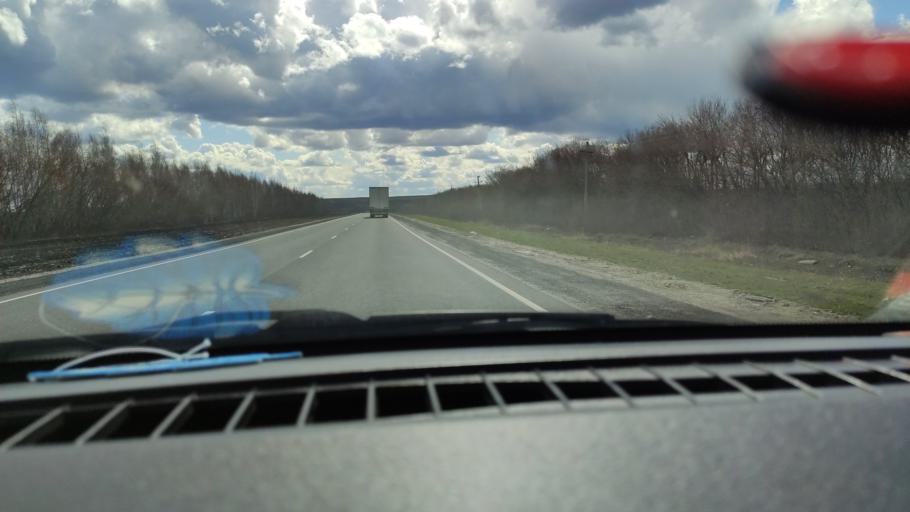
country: RU
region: Samara
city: Varlamovo
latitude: 52.9797
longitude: 48.3120
